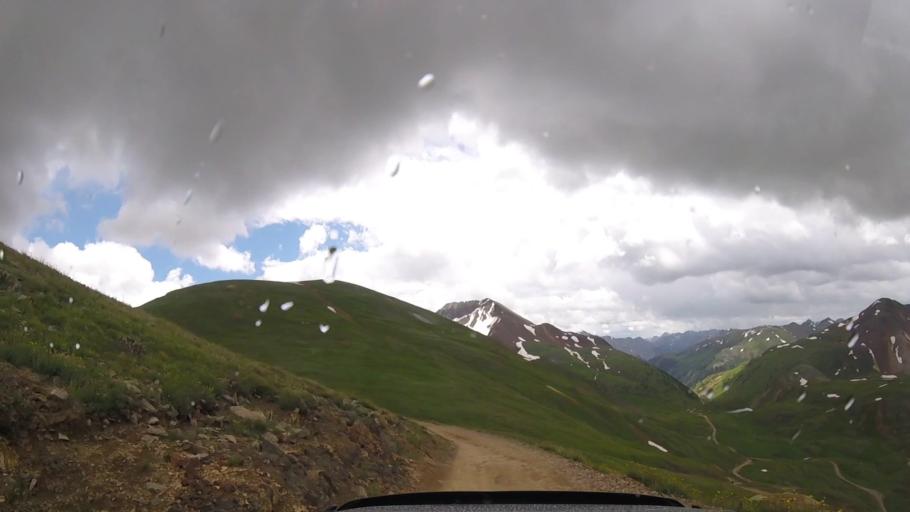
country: US
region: Colorado
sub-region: Ouray County
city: Ouray
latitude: 37.9640
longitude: -107.5755
